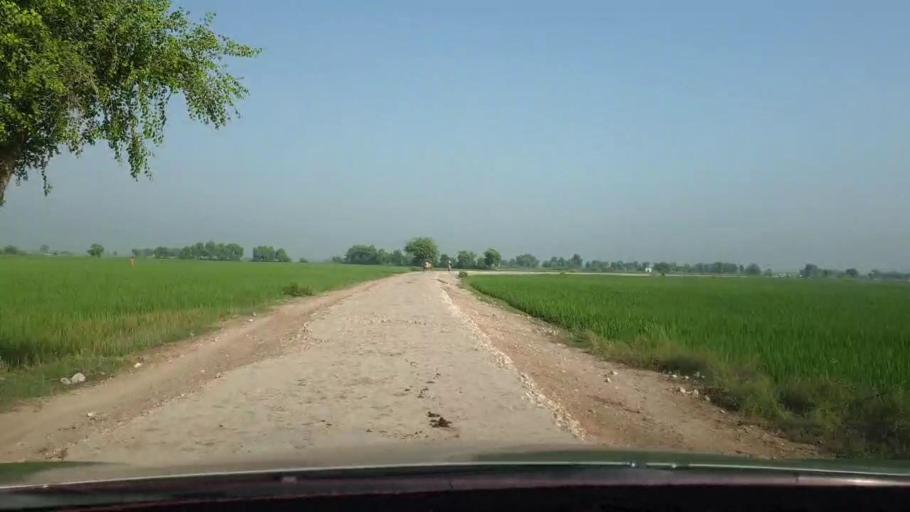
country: PK
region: Sindh
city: Nasirabad
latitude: 27.4292
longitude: 67.9211
